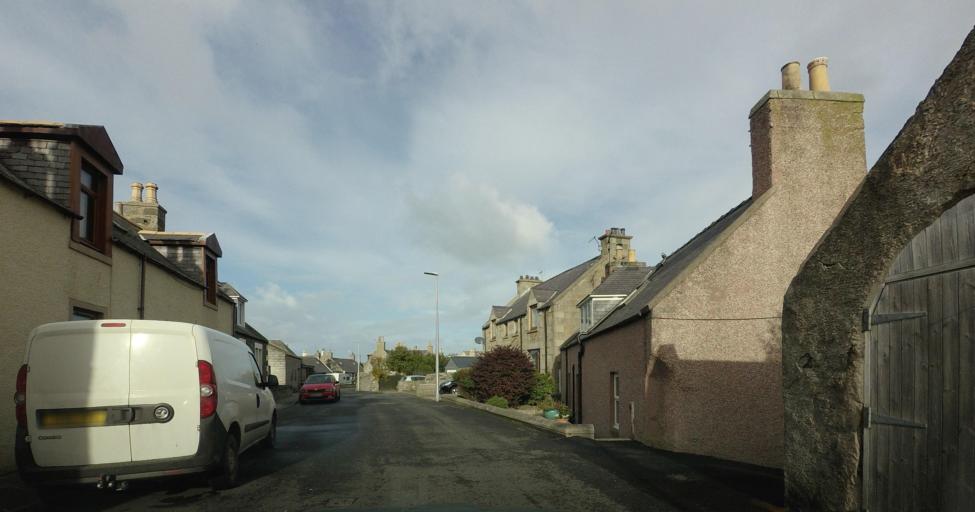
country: GB
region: Scotland
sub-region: Aberdeenshire
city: Portsoy
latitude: 57.6823
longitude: -2.6934
